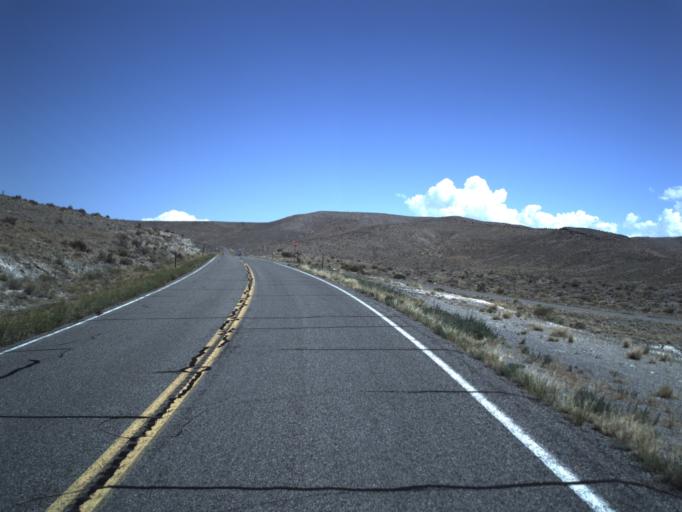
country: US
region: Utah
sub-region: Beaver County
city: Milford
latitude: 39.0229
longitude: -113.3642
